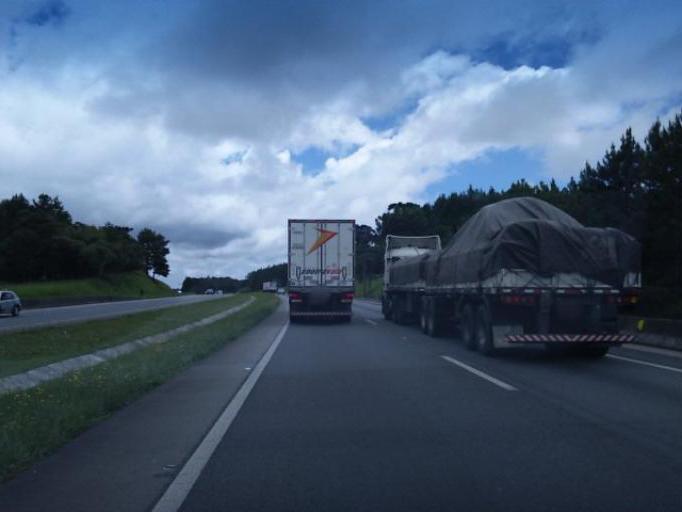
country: BR
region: Parana
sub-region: Piraquara
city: Piraquara
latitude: -25.4736
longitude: -49.0937
